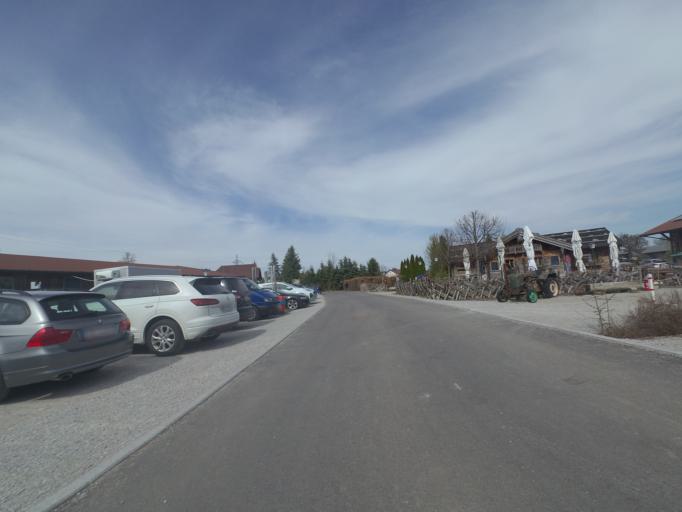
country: DE
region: Bavaria
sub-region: Upper Bavaria
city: Ainring
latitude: 47.8070
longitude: 12.9799
